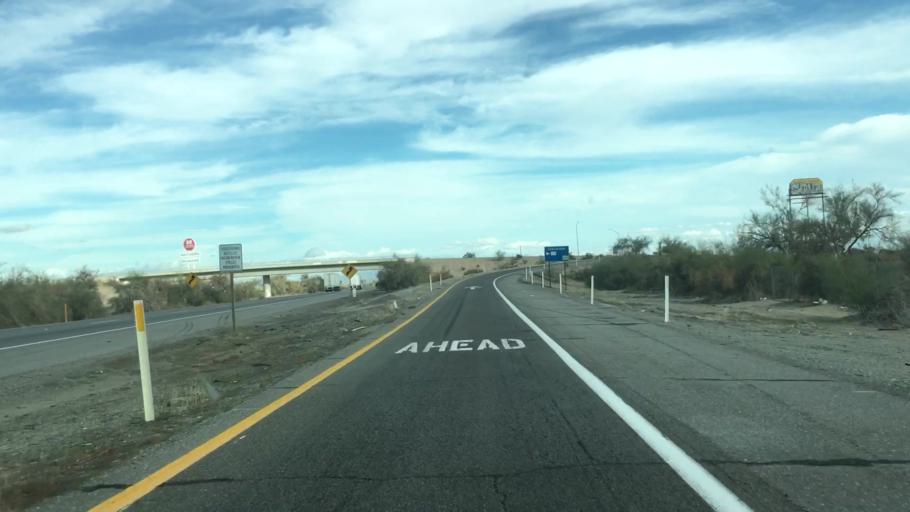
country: US
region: California
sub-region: Riverside County
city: Mesa Verde
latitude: 33.6090
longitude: -114.7298
